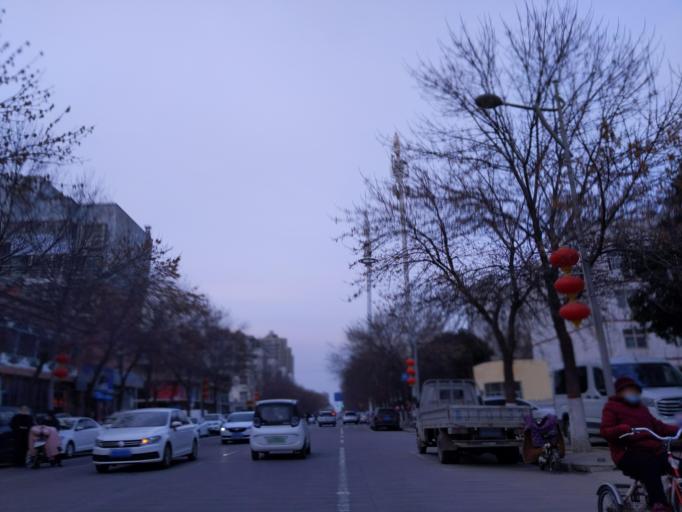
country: CN
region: Henan Sheng
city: Zhongyuanlu
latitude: 35.7834
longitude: 115.0391
